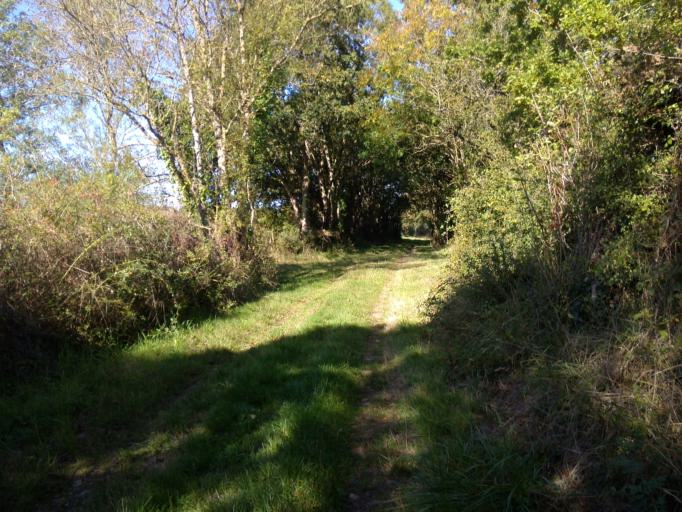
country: FR
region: Pays de la Loire
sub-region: Departement de la Loire-Atlantique
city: Chemere
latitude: 47.1096
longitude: -1.9233
